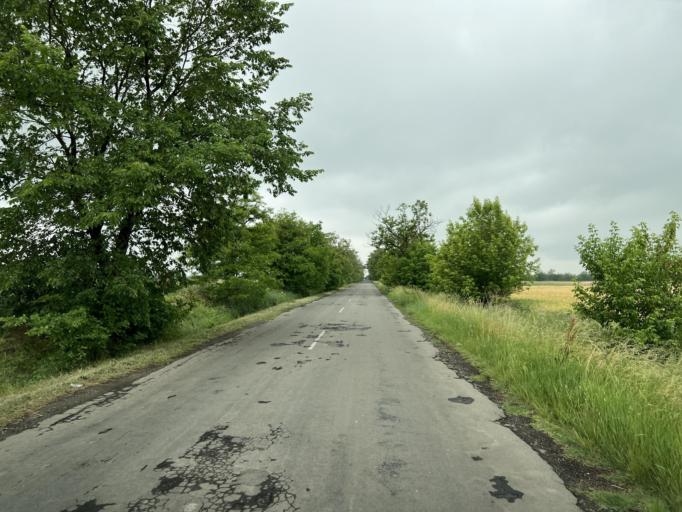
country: HU
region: Pest
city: Tura
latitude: 47.6217
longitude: 19.6256
